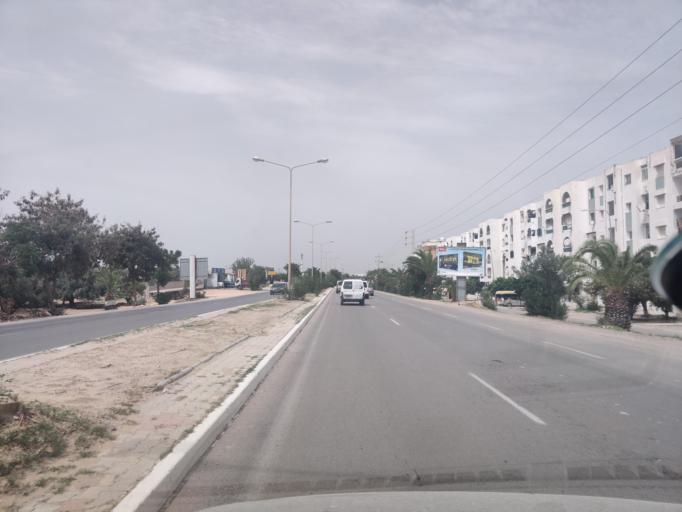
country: TN
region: Susah
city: Hammam Sousse
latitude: 35.8377
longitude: 10.5858
